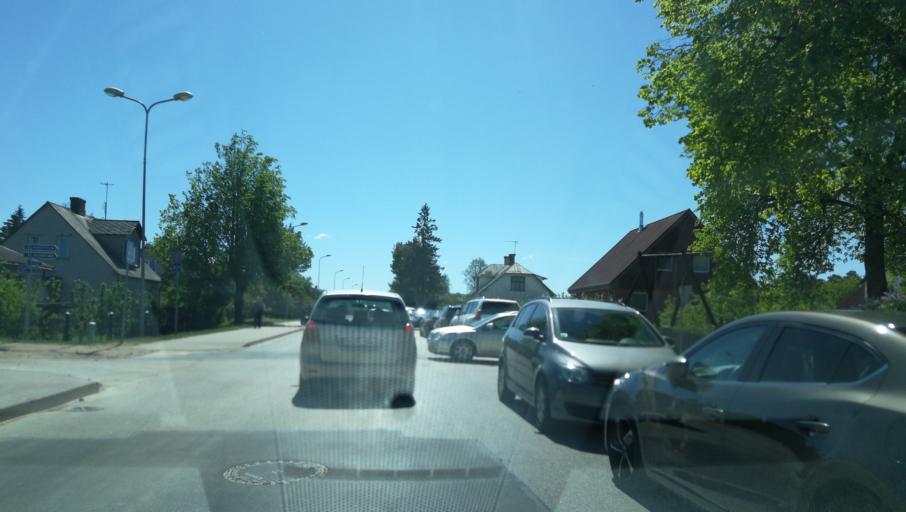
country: LV
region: Dobeles Rajons
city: Dobele
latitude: 56.6122
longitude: 23.2925
